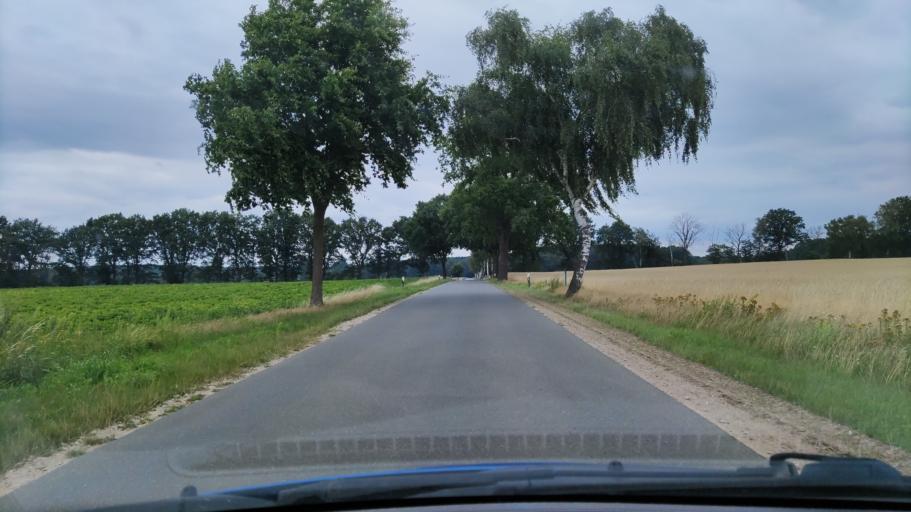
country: DE
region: Lower Saxony
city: Rosche
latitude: 53.0201
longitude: 10.7291
